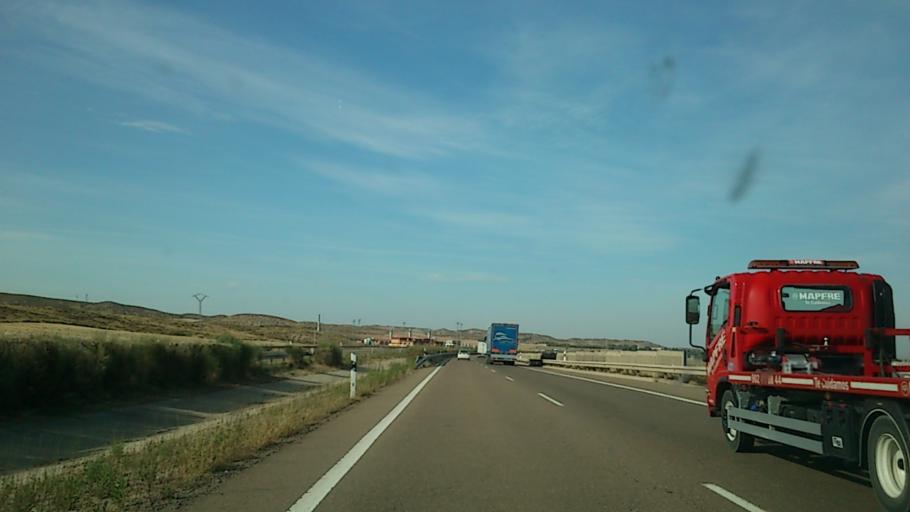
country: ES
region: Aragon
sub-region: Provincia de Zaragoza
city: Cadrete
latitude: 41.5733
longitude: -0.9616
